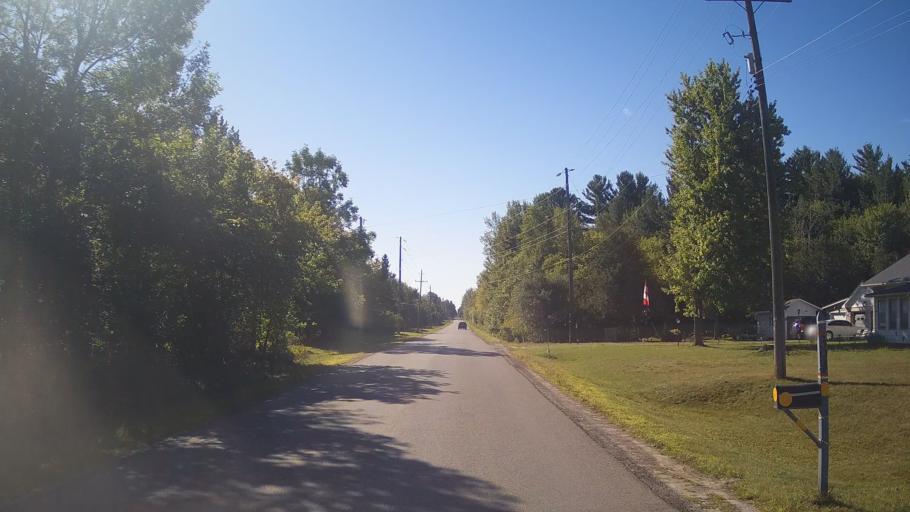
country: CA
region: Ontario
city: Prescott
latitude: 45.0215
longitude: -75.6196
